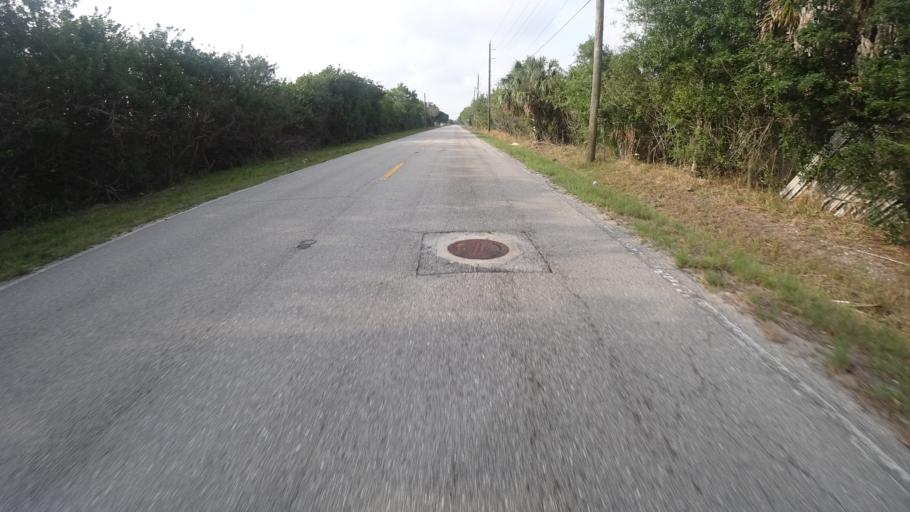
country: US
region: Florida
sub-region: Manatee County
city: Whitfield
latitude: 27.4248
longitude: -82.5219
